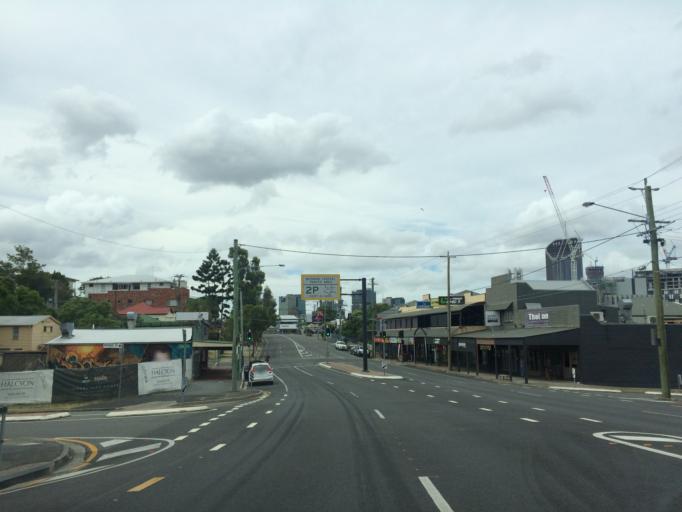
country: AU
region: Queensland
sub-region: Brisbane
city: South Brisbane
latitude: -27.4853
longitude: 153.0196
